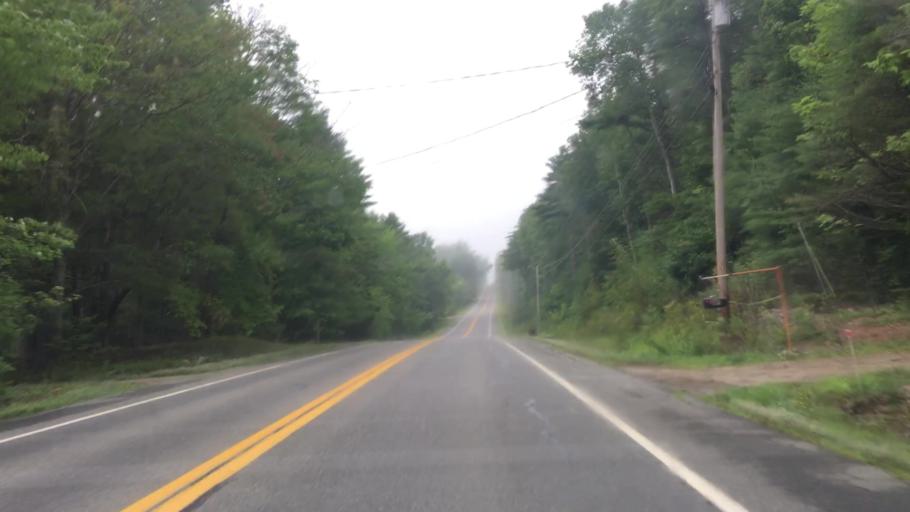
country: US
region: Maine
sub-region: Lincoln County
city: Wiscasset
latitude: 44.0605
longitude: -69.6877
